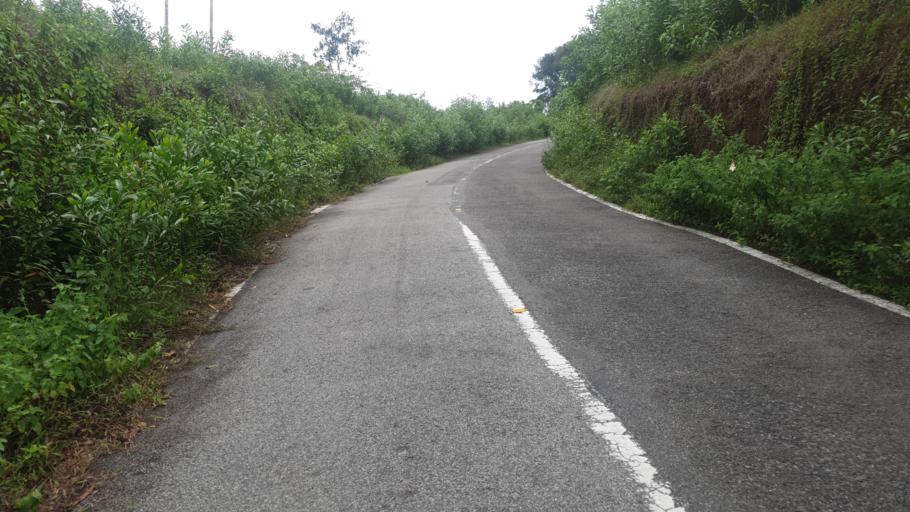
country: IN
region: Kerala
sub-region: Thiruvananthapuram
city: Nedumangad
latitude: 8.6417
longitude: 77.1091
